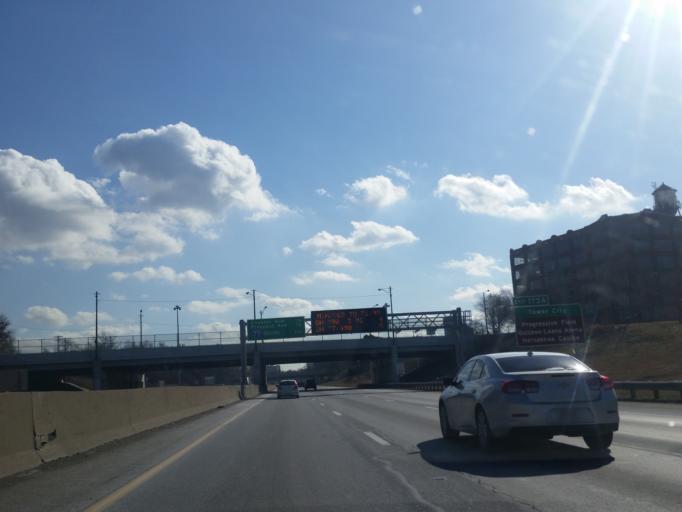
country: US
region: Ohio
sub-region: Cuyahoga County
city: Cleveland
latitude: 41.5112
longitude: -81.6725
